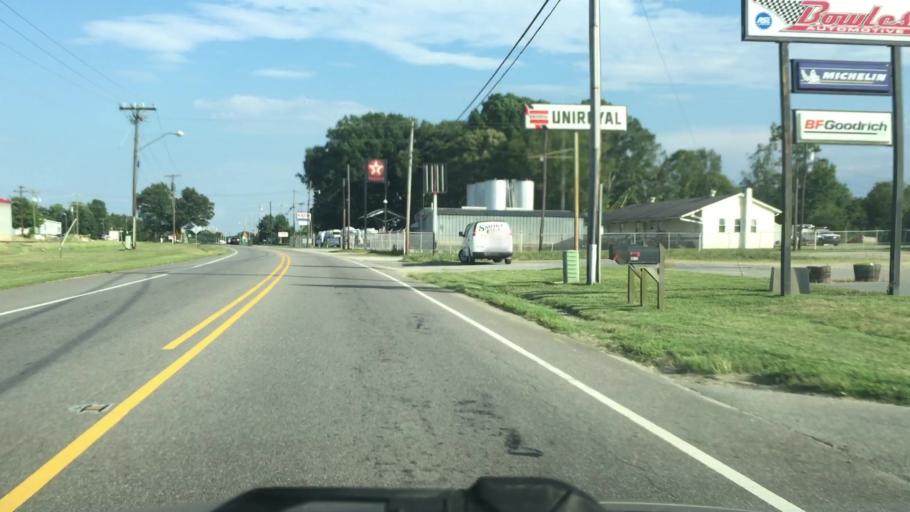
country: US
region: North Carolina
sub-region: Iredell County
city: Mooresville
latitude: 35.6030
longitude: -80.8138
